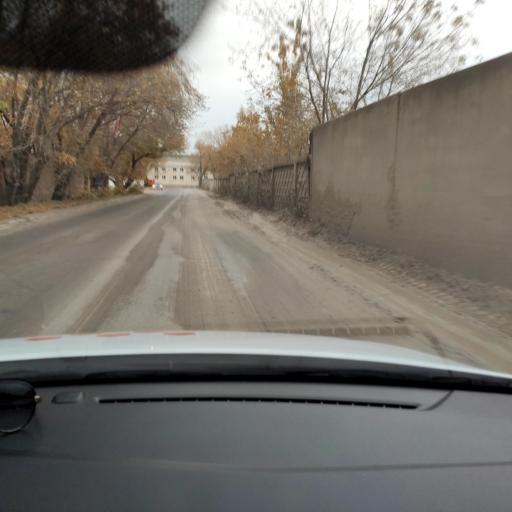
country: RU
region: Tatarstan
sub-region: Gorod Kazan'
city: Kazan
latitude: 55.7442
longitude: 49.1023
